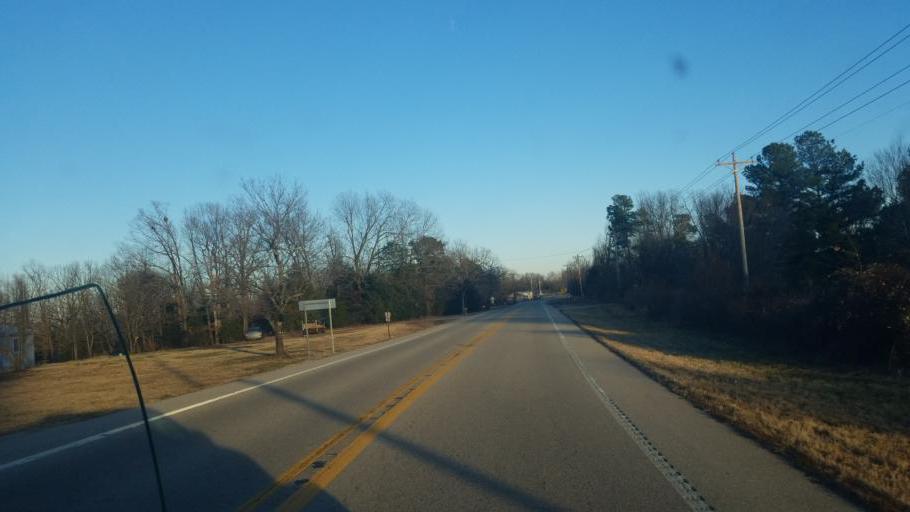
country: US
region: Arkansas
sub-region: Baxter County
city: Mountain Home
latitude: 36.3847
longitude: -92.1651
